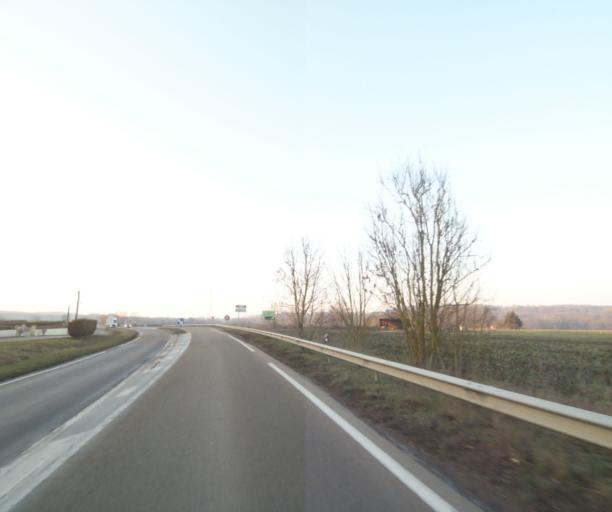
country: FR
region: Lorraine
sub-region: Departement de la Meuse
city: Ancerville
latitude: 48.6045
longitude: 5.0289
